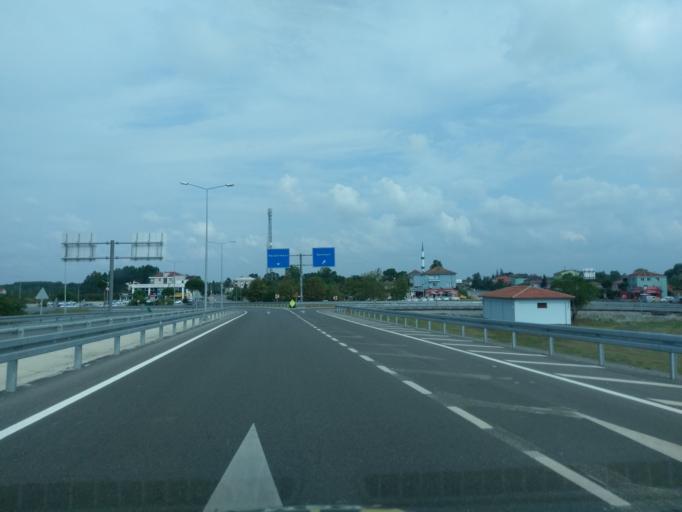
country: TR
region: Samsun
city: Dikbiyik
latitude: 41.2379
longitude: 36.5375
